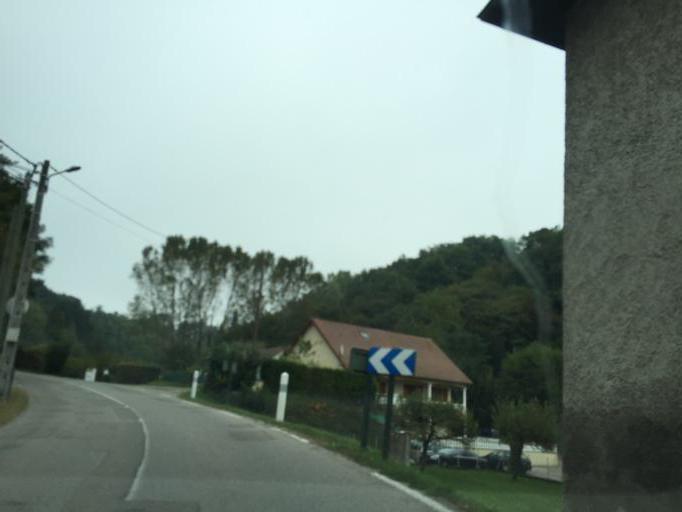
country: FR
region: Rhone-Alpes
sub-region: Departement de l'Isere
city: Saint-Clair-de-la-Tour
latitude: 45.5746
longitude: 5.4811
